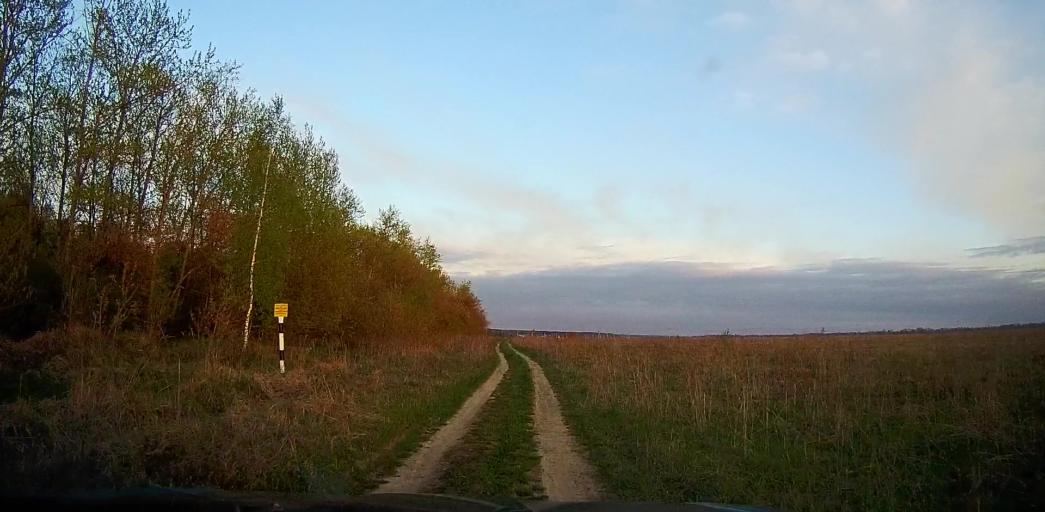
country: RU
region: Moskovskaya
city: Peski
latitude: 55.2335
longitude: 38.7293
